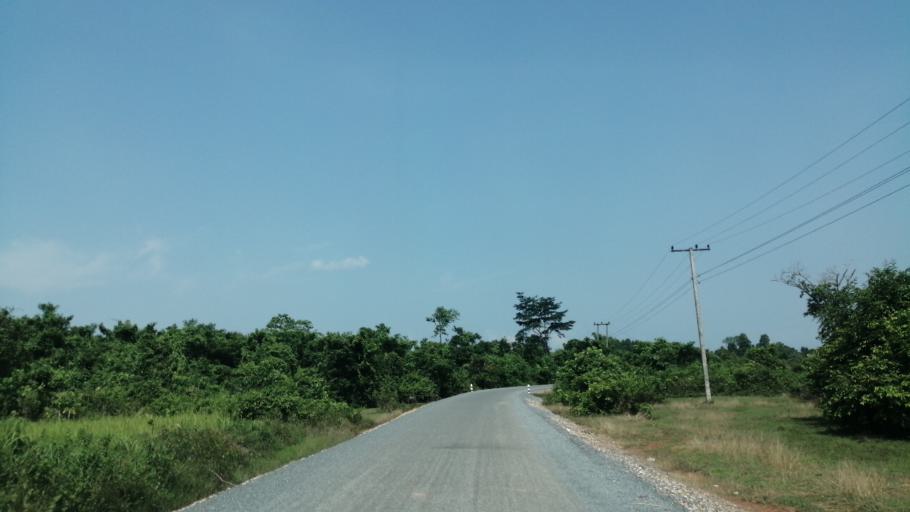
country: LA
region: Bolikhamxai
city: Bolikhan
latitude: 18.4494
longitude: 103.8102
